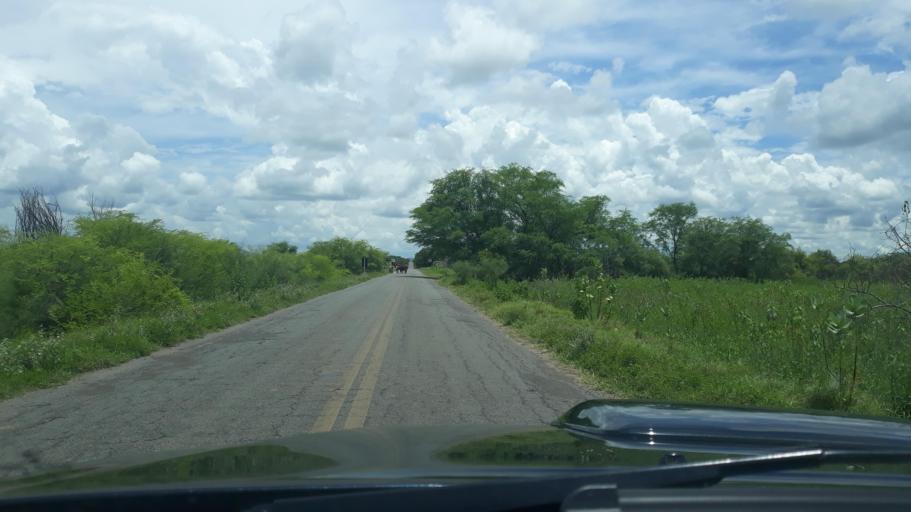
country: BR
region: Bahia
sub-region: Guanambi
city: Guanambi
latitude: -13.9130
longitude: -42.8436
